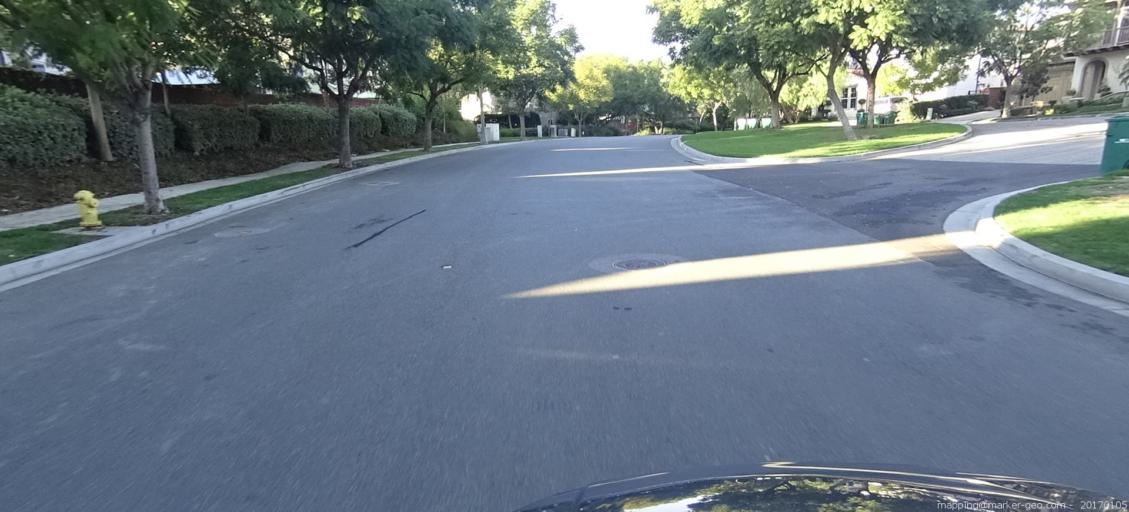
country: US
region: California
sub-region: Orange County
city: Ladera Ranch
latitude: 33.5505
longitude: -117.6406
